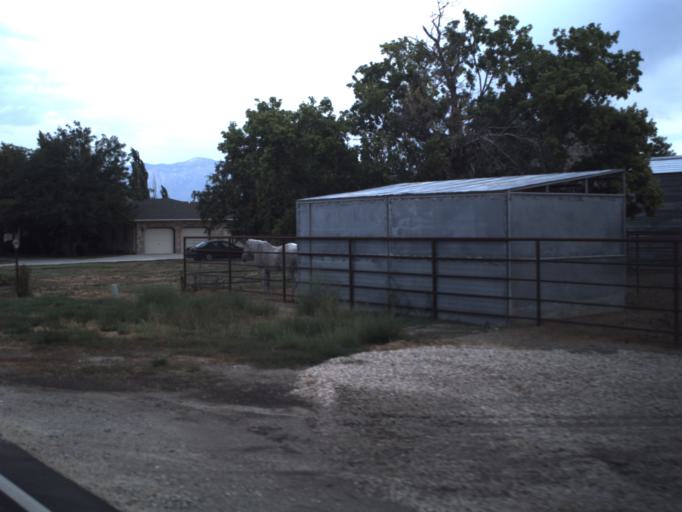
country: US
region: Utah
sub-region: Weber County
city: West Haven
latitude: 41.2168
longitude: -112.0929
